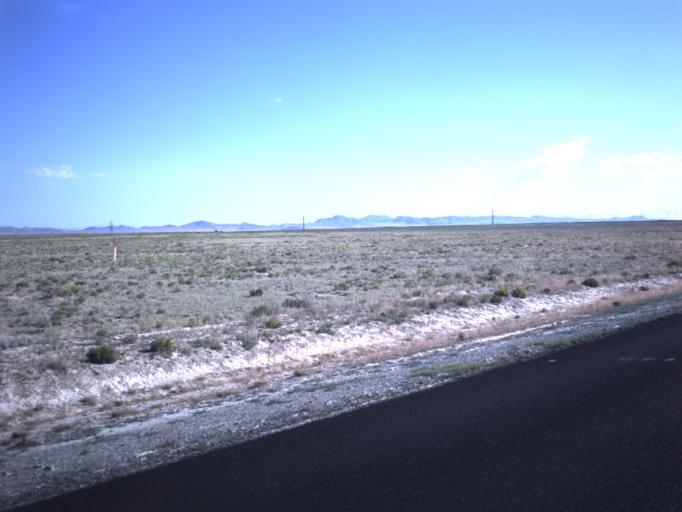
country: US
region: Utah
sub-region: Beaver County
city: Milford
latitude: 38.4726
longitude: -112.9938
